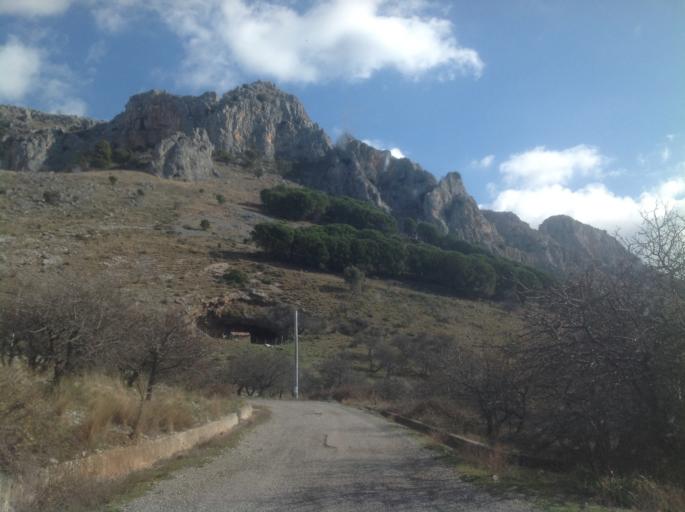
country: IT
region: Calabria
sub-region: Provincia di Cosenza
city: Frascineto
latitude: 39.8416
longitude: 16.2605
